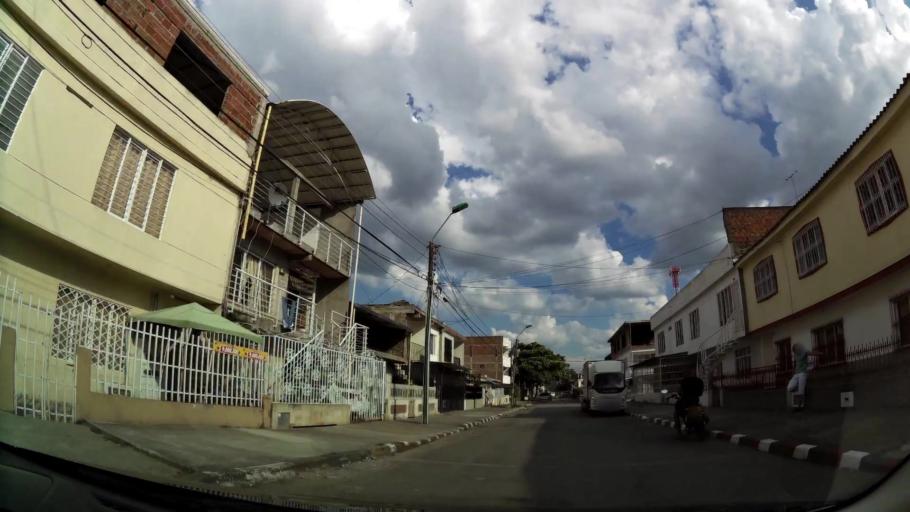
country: CO
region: Valle del Cauca
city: Cali
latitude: 3.4092
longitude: -76.5127
